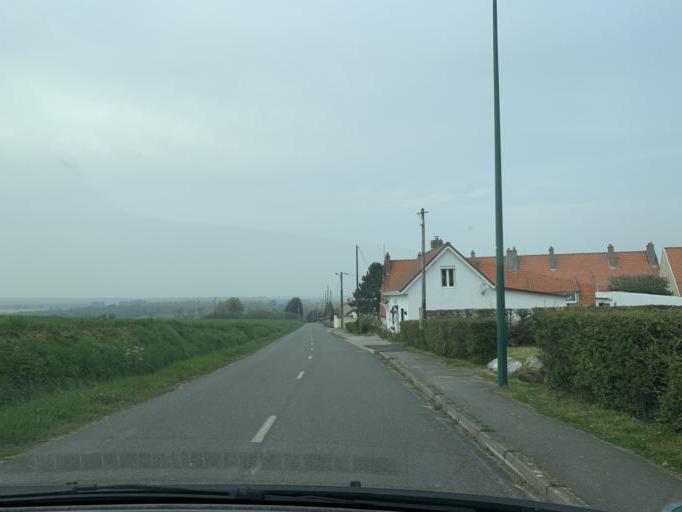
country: FR
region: Nord-Pas-de-Calais
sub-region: Departement du Pas-de-Calais
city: Samer
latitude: 50.6460
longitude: 1.7517
